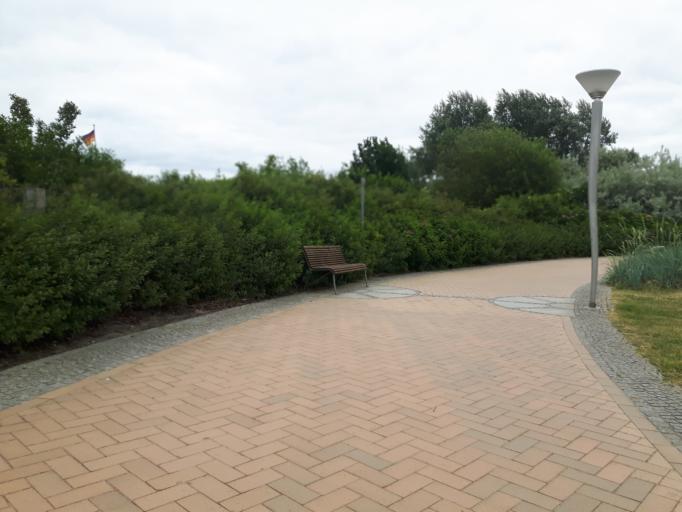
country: DE
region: Schleswig-Holstein
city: Schashagen
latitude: 54.0866
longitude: 10.8629
